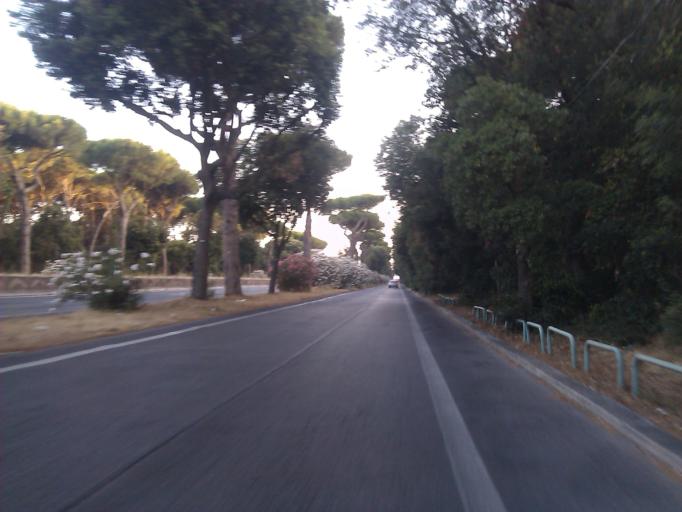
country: IT
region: Latium
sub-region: Citta metropolitana di Roma Capitale
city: Acilia-Castel Fusano-Ostia Antica
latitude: 41.7216
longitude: 12.3261
